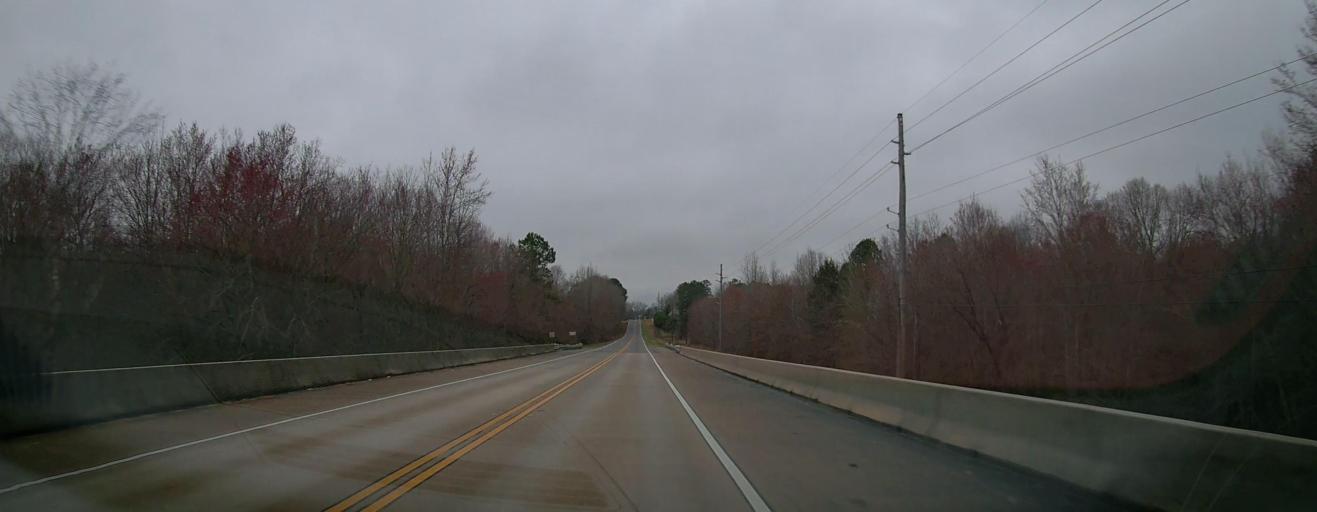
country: US
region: Georgia
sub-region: Pike County
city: Zebulon
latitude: 33.1029
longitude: -84.3612
